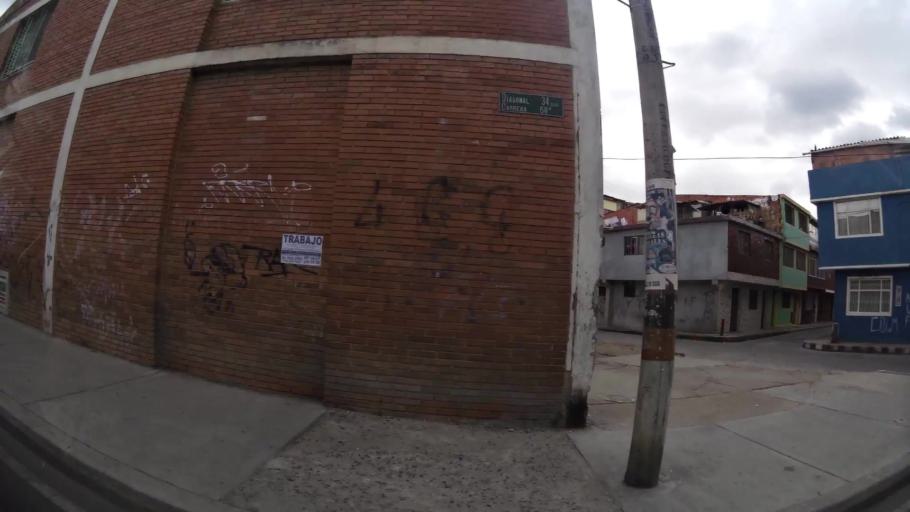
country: CO
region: Bogota D.C.
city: Bogota
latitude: 4.6063
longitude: -74.1327
